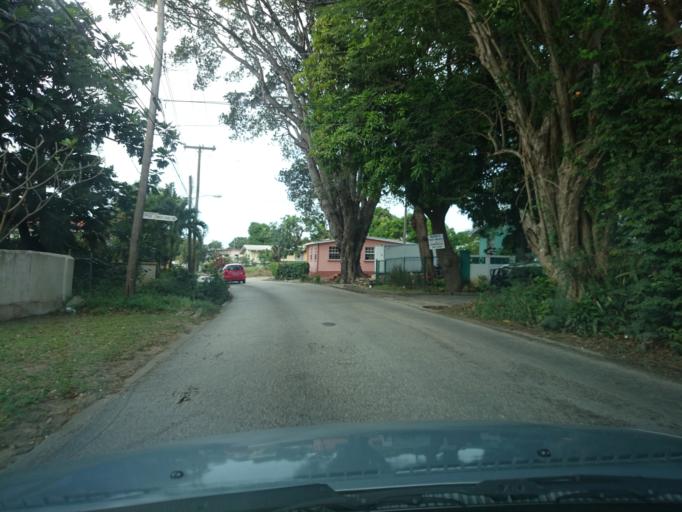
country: BB
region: Saint Peter
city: Speightstown
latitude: 13.2219
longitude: -59.6411
